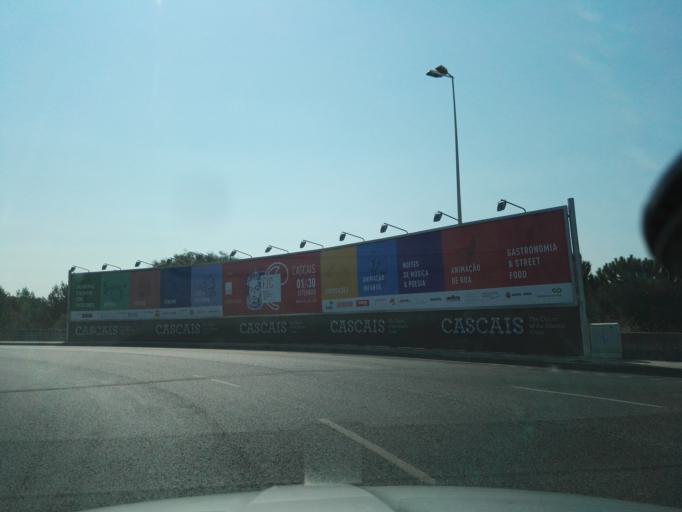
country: PT
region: Lisbon
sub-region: Cascais
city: Estoril
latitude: 38.7152
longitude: -9.3890
